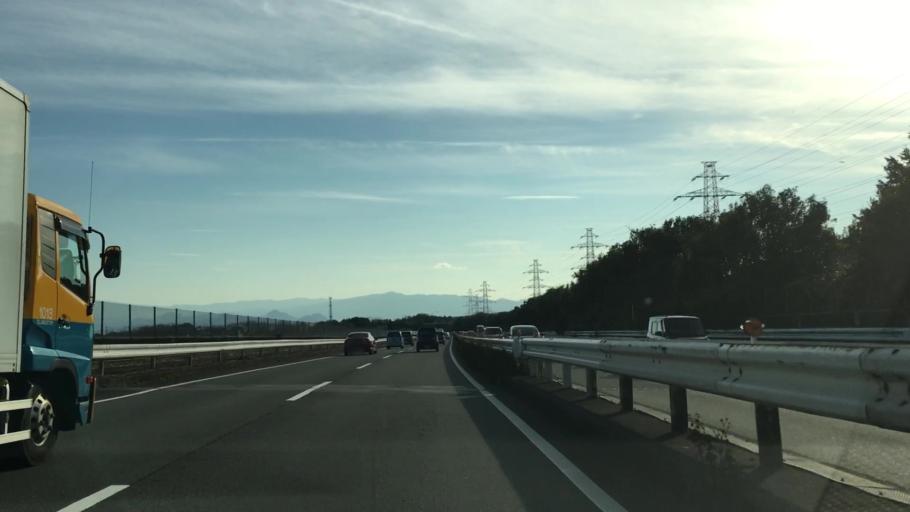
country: JP
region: Shizuoka
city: Gotemba
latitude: 35.2476
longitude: 138.9106
